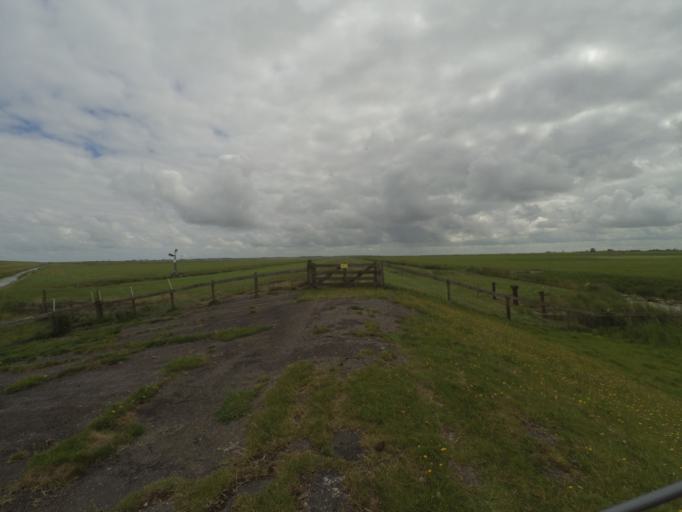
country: NL
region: Friesland
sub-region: Gemeente Dongeradeel
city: Anjum
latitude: 53.4029
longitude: 6.1398
